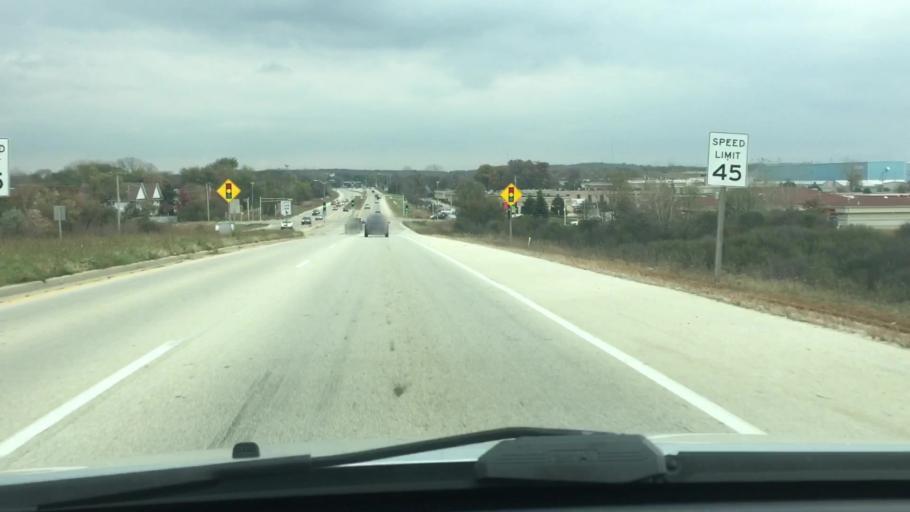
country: US
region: Wisconsin
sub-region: Waukesha County
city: Waukesha
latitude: 42.9770
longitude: -88.2387
